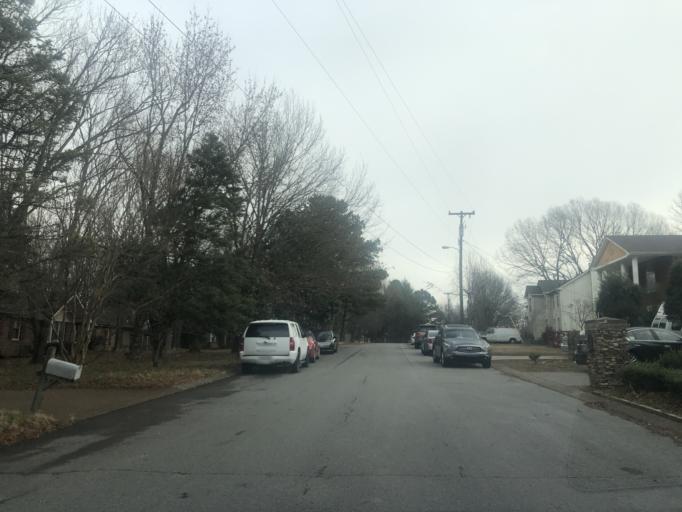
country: US
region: Tennessee
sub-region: Rutherford County
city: La Vergne
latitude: 36.0738
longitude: -86.6565
